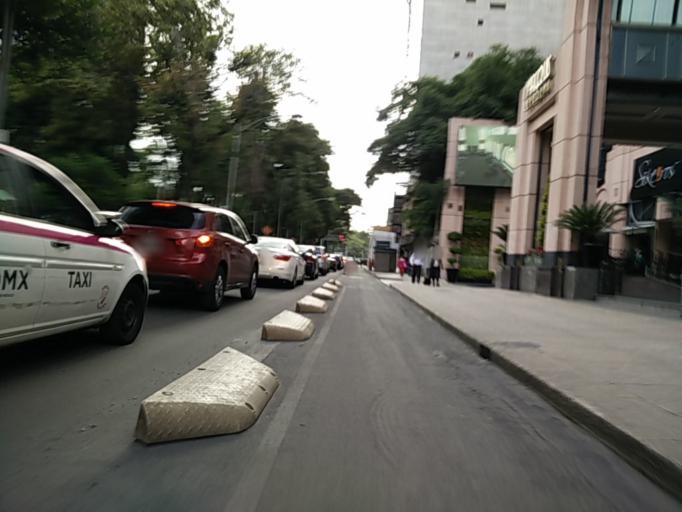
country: MX
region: Mexico City
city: Polanco
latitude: 19.4248
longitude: -99.1735
